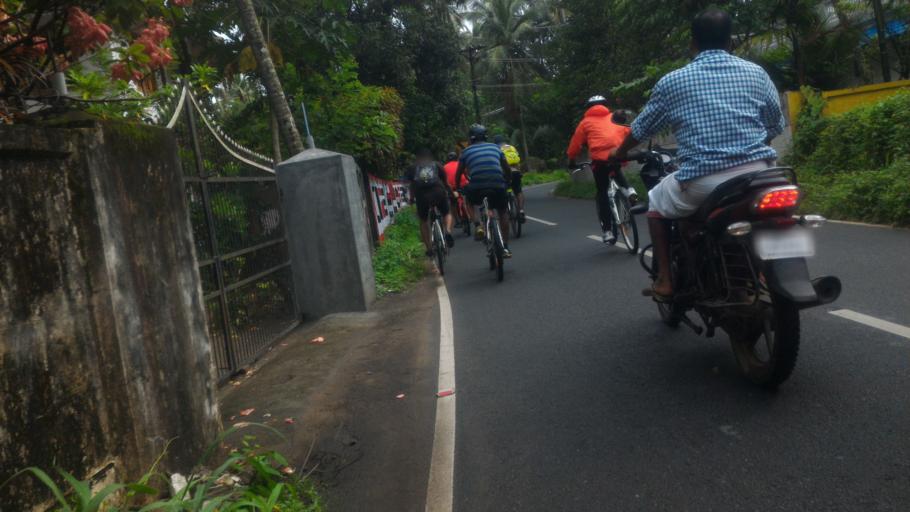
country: IN
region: Kerala
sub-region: Thrissur District
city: Thanniyam
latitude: 10.4376
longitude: 76.0819
